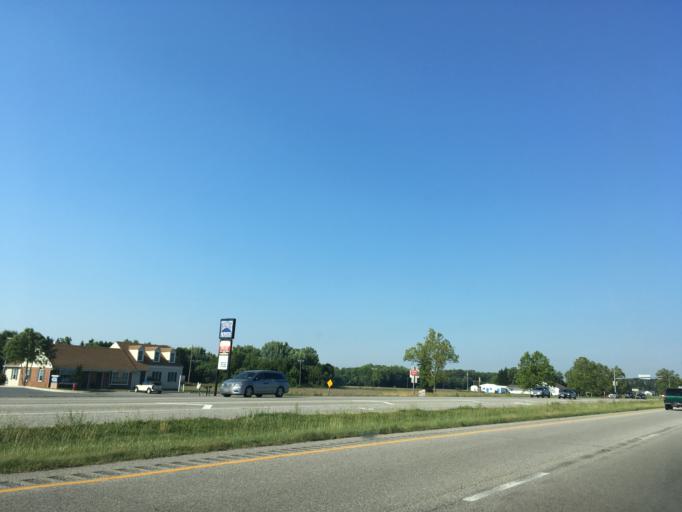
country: US
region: Maryland
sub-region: Queen Anne's County
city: Grasonville
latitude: 38.9876
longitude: -76.1524
